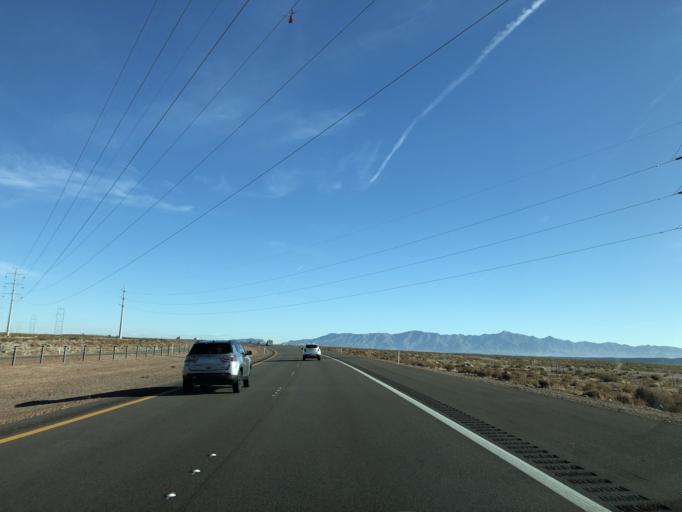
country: US
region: Nevada
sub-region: Clark County
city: Boulder City
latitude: 35.9414
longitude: -114.8145
